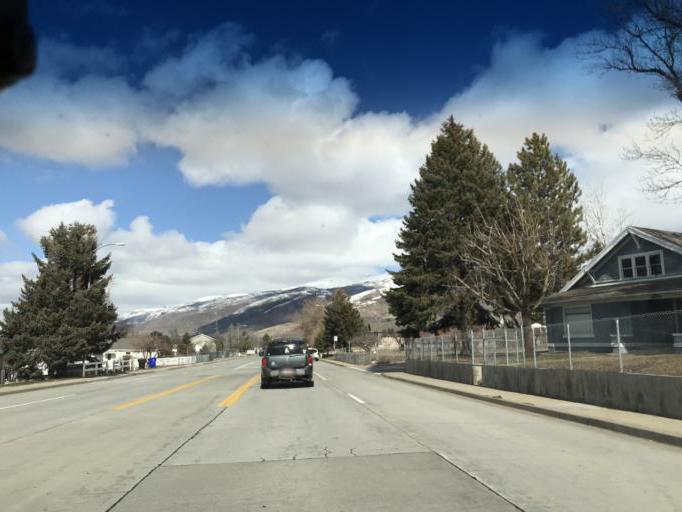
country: US
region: Utah
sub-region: Davis County
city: Woods Cross
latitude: 40.8725
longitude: -111.8760
